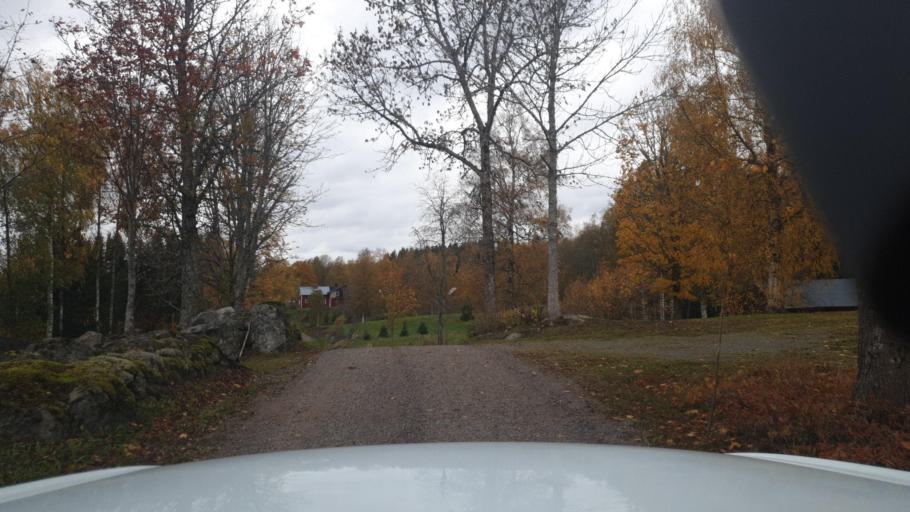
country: SE
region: Vaermland
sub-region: Torsby Kommun
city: Torsby
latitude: 59.9556
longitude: 12.7293
